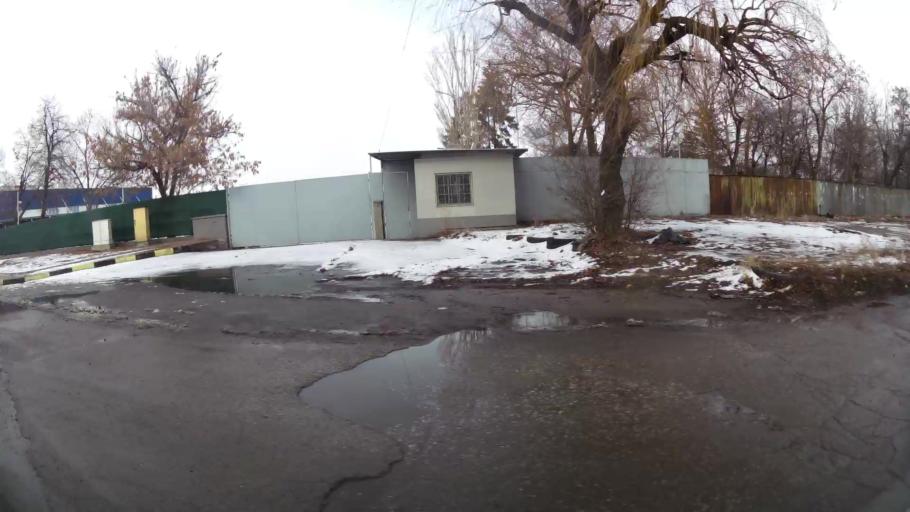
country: BG
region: Sofia-Capital
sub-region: Stolichna Obshtina
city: Sofia
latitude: 42.6933
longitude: 23.3797
